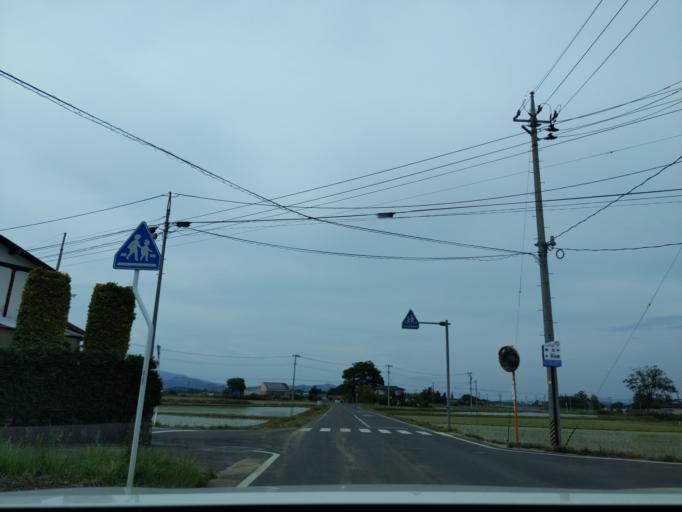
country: JP
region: Fukushima
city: Koriyama
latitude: 37.4005
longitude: 140.3062
